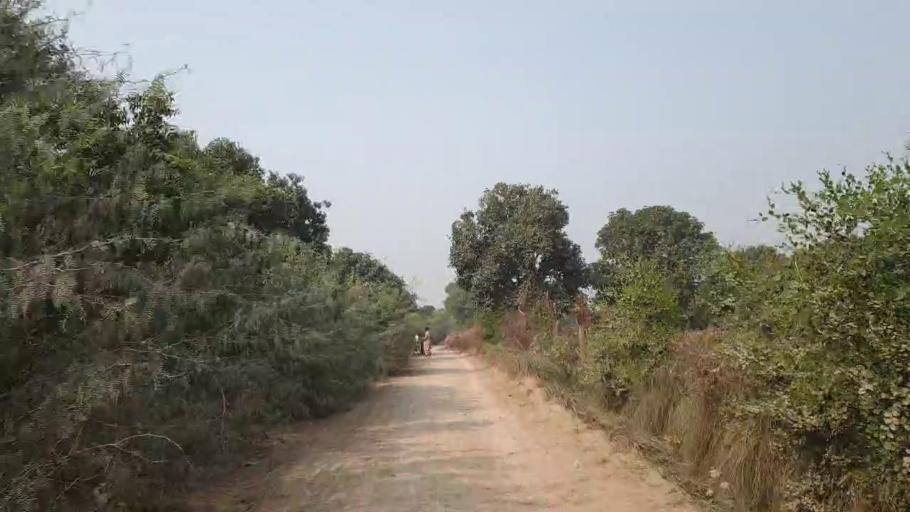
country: PK
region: Sindh
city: Tando Muhammad Khan
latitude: 25.2061
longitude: 68.5612
